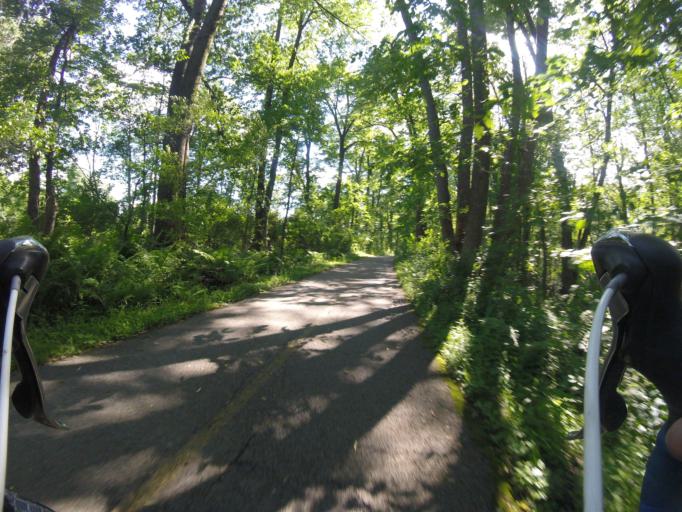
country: CA
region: Quebec
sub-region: Outaouais
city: Gatineau
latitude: 45.4513
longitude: -75.7126
